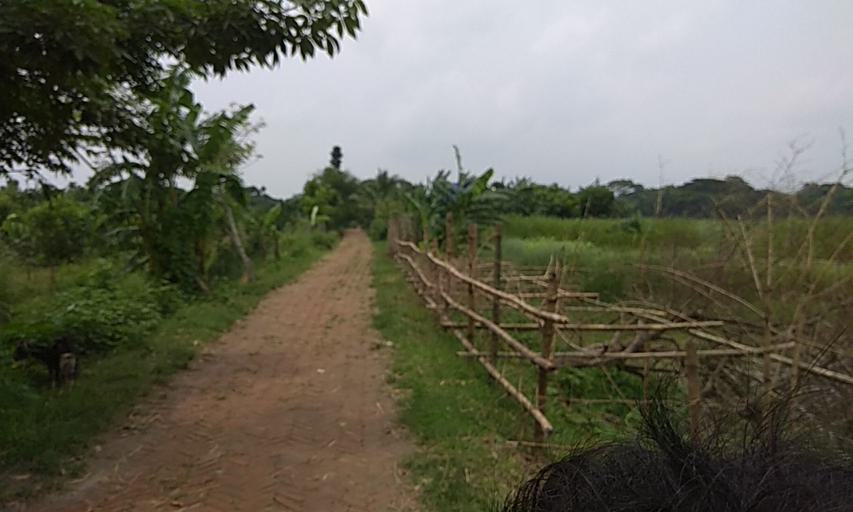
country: BD
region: Dhaka
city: Dohar
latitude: 23.5396
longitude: 89.9914
